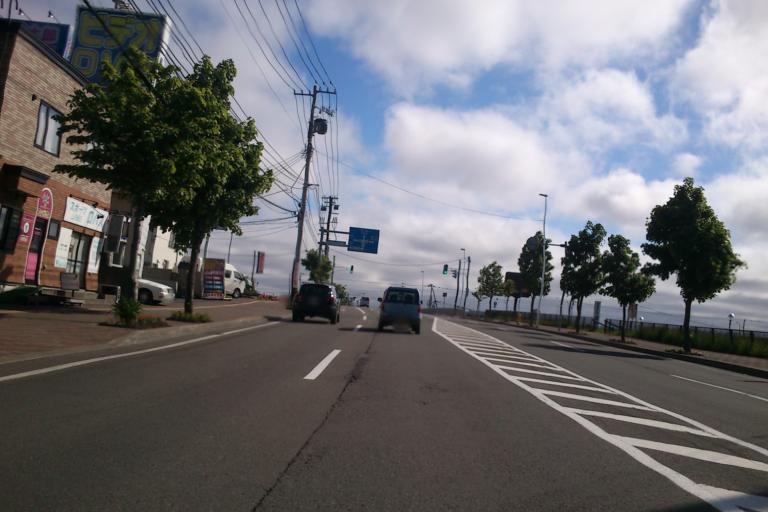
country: JP
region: Hokkaido
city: Sapporo
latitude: 43.1322
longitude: 141.2621
